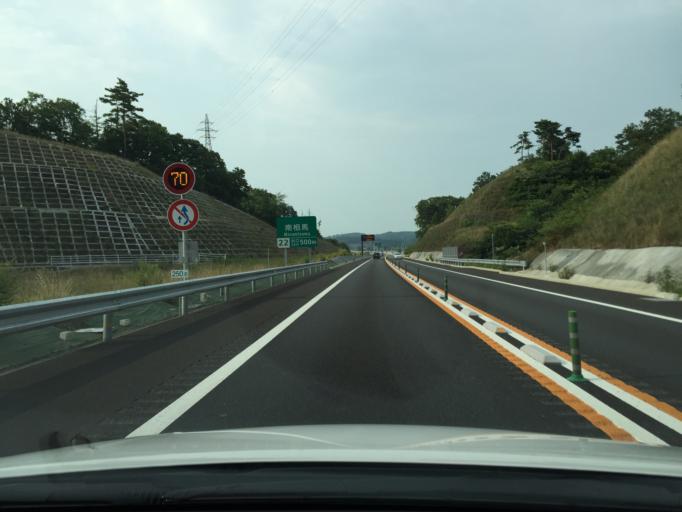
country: JP
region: Fukushima
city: Namie
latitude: 37.6521
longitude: 140.9179
